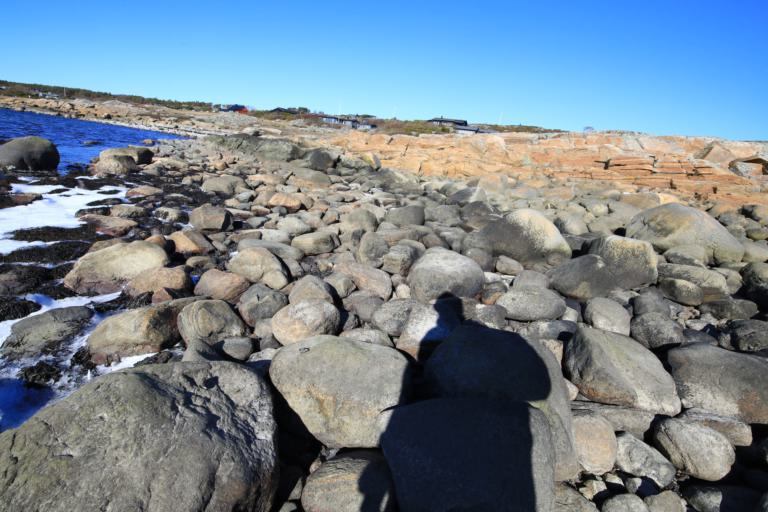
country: SE
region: Halland
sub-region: Kungsbacka Kommun
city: Frillesas
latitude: 57.2265
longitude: 12.1194
